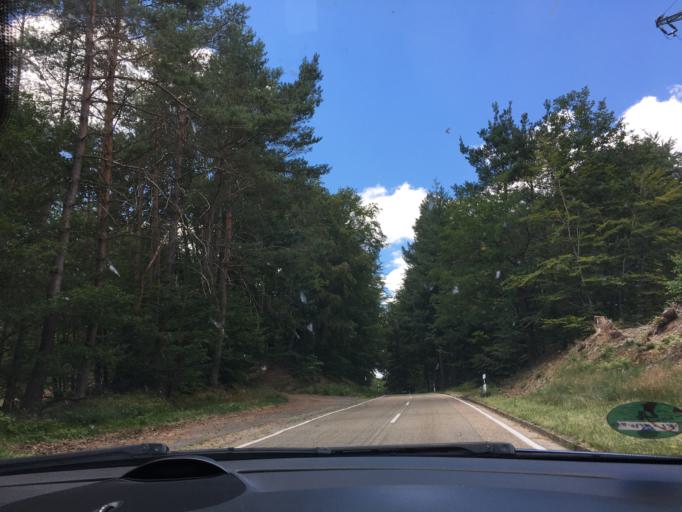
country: DE
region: Rheinland-Pfalz
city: Hauenstein
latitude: 49.2129
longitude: 7.8391
